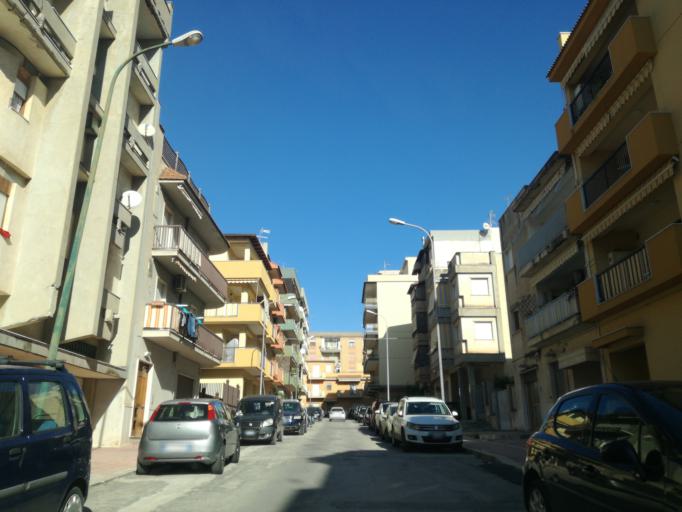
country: IT
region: Sicily
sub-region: Provincia di Caltanissetta
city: Gela
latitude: 37.0720
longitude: 14.2323
